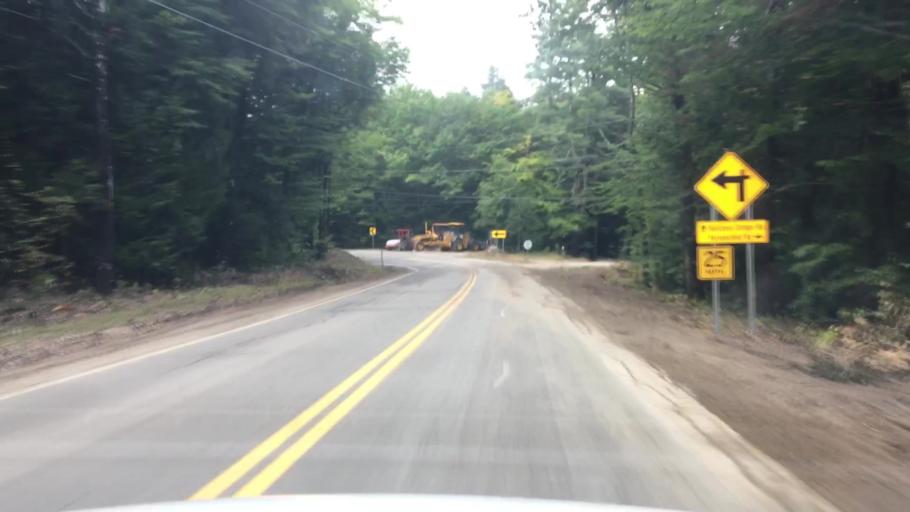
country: US
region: New Hampshire
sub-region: Carroll County
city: Effingham
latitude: 43.7760
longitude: -70.9995
